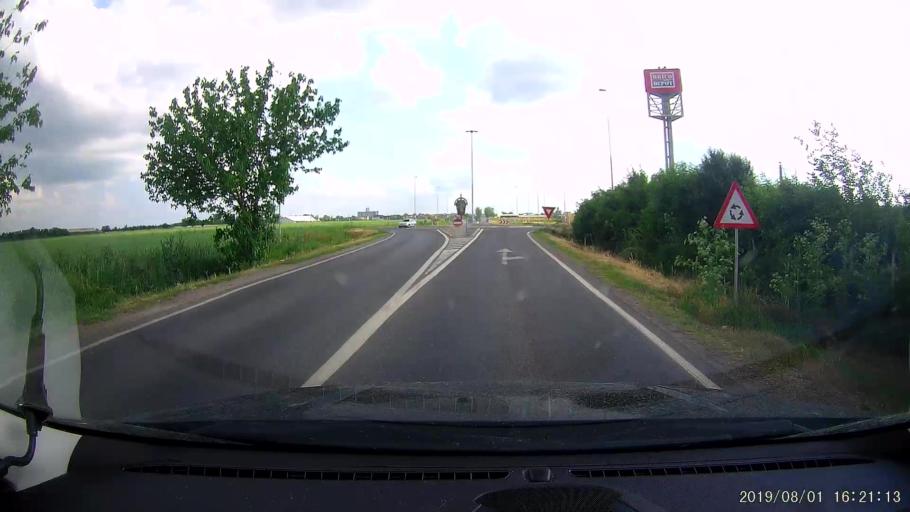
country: RO
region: Calarasi
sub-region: Municipiul Calarasi
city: Calarasi
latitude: 44.2194
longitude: 27.3404
